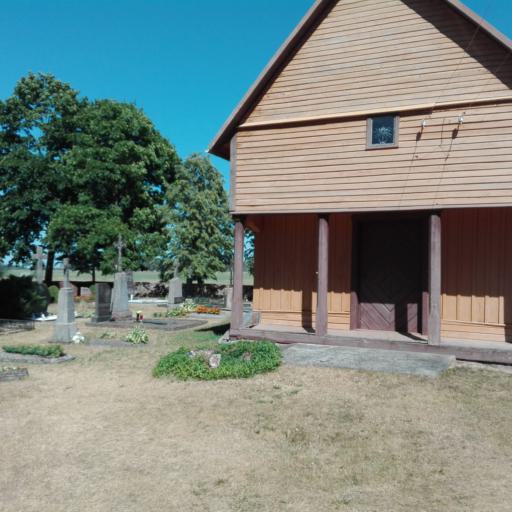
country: LT
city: Vabalninkas
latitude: 55.9749
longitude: 24.6664
